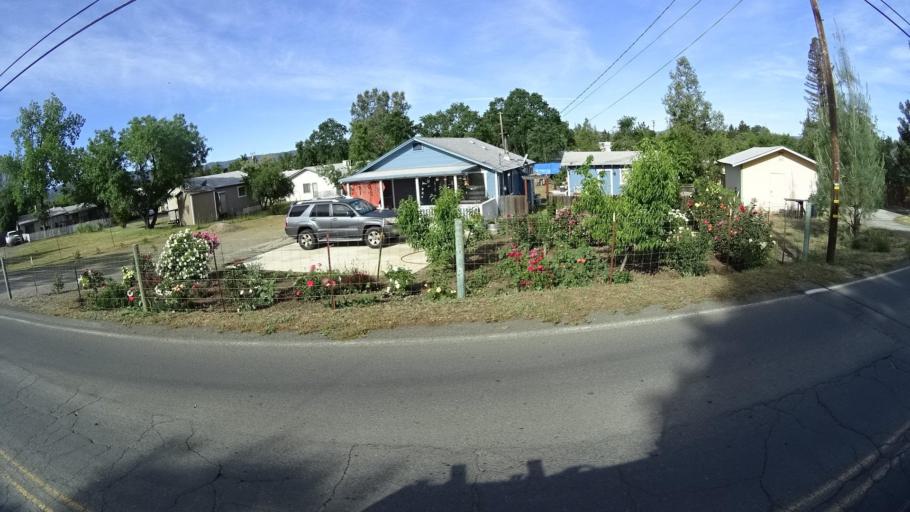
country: US
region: California
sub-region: Lake County
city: Kelseyville
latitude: 38.9734
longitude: -122.8308
